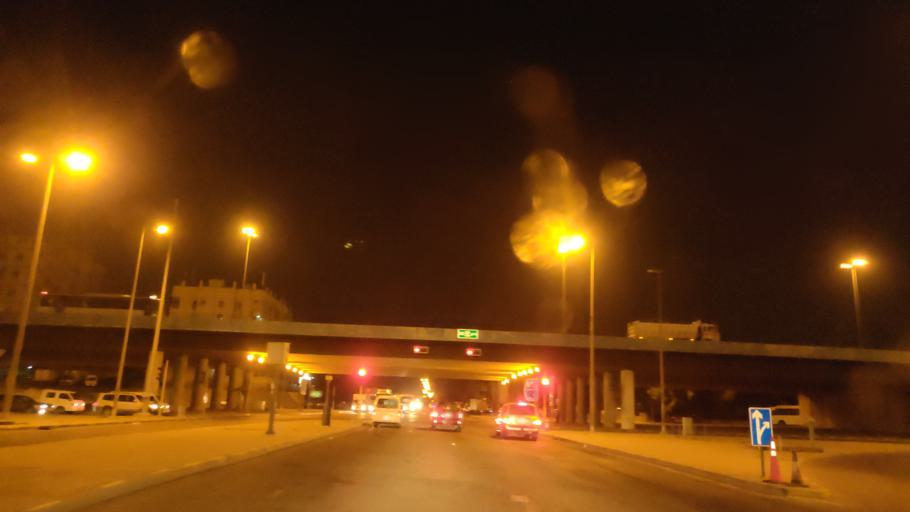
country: KW
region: Al Farwaniyah
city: Al Farwaniyah
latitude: 29.2676
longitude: 47.9400
